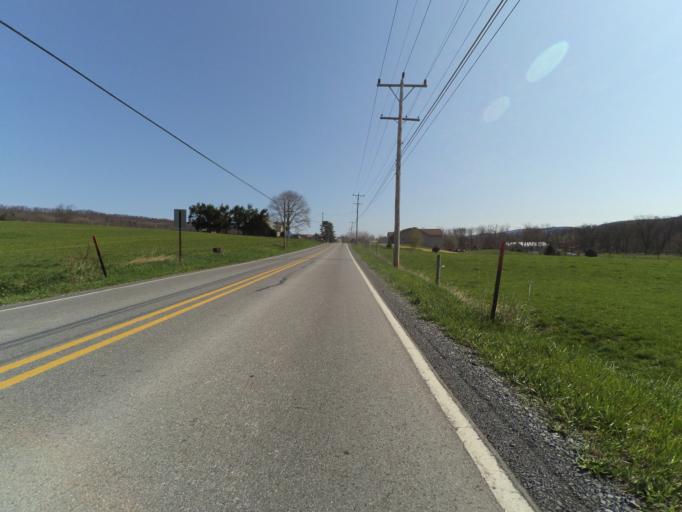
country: US
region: Pennsylvania
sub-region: Centre County
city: Zion
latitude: 40.9805
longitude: -77.5916
